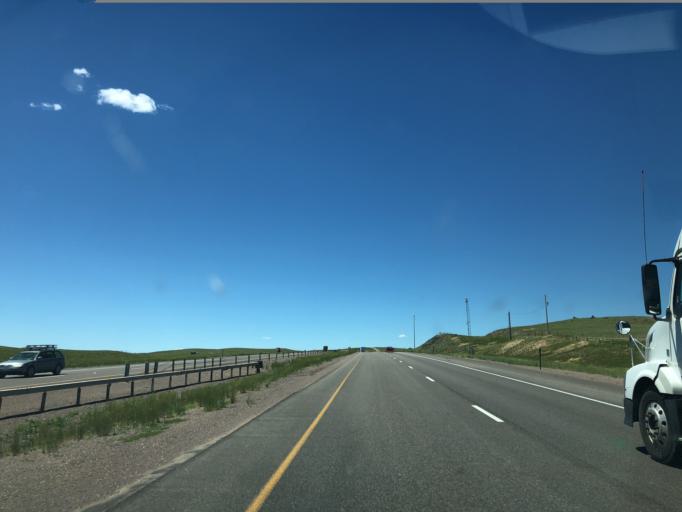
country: US
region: Wyoming
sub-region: Laramie County
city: Cheyenne
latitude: 41.0977
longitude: -105.2080
